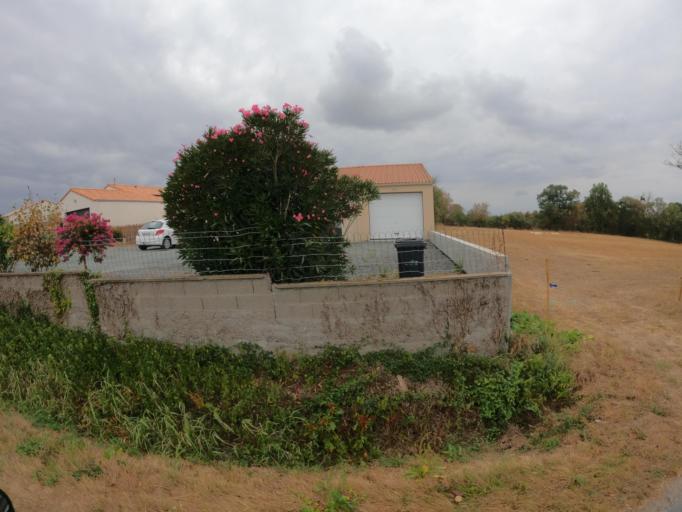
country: FR
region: Pays de la Loire
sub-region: Departement de la Vendee
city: Les Landes-Genusson
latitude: 46.9687
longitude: -1.1155
